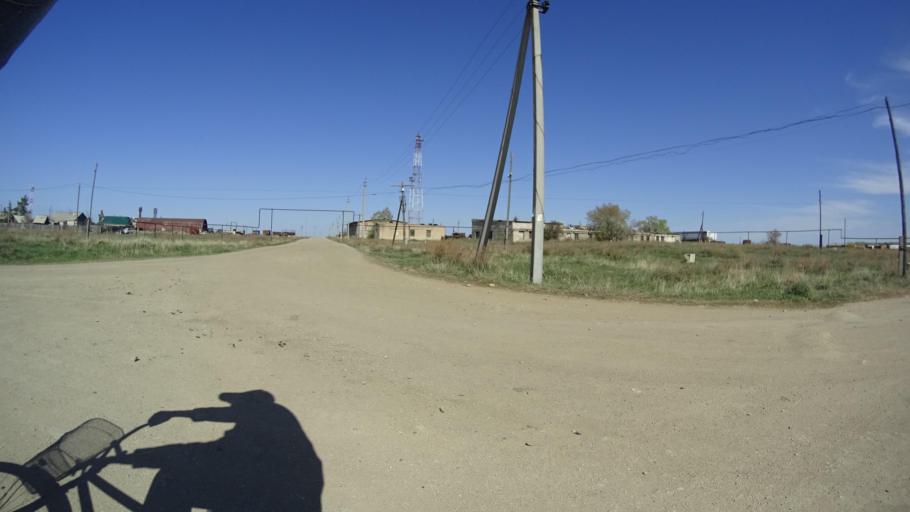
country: RU
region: Chelyabinsk
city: Chesma
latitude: 53.7884
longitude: 61.0387
